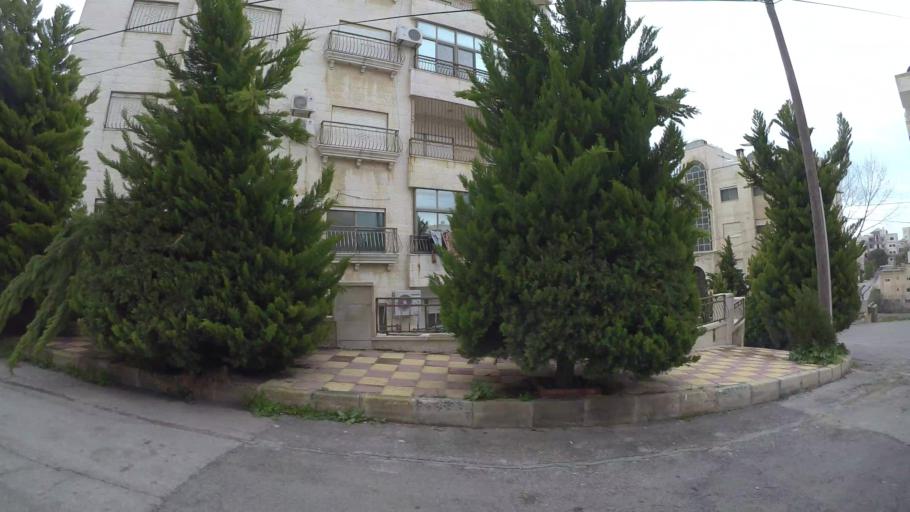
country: JO
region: Amman
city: Wadi as Sir
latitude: 31.9676
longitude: 35.8319
